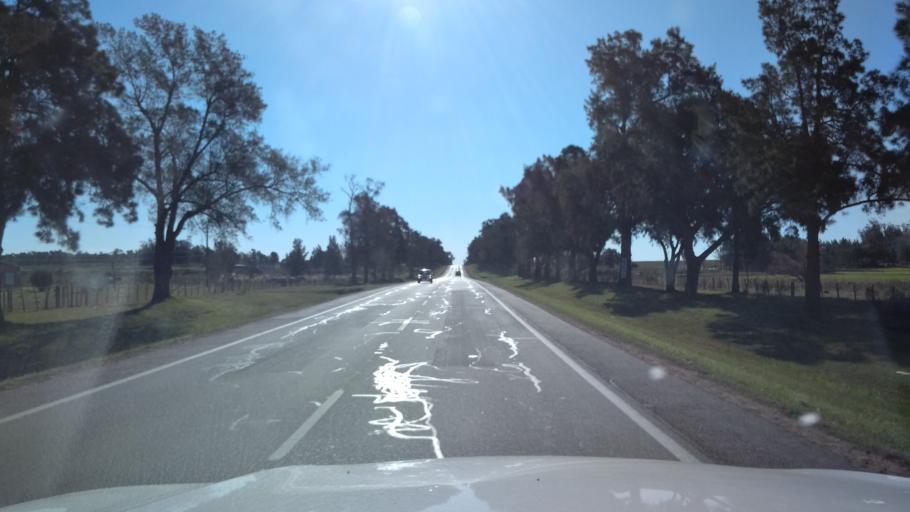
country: UY
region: Canelones
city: San Jacinto
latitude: -34.5936
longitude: -55.8336
